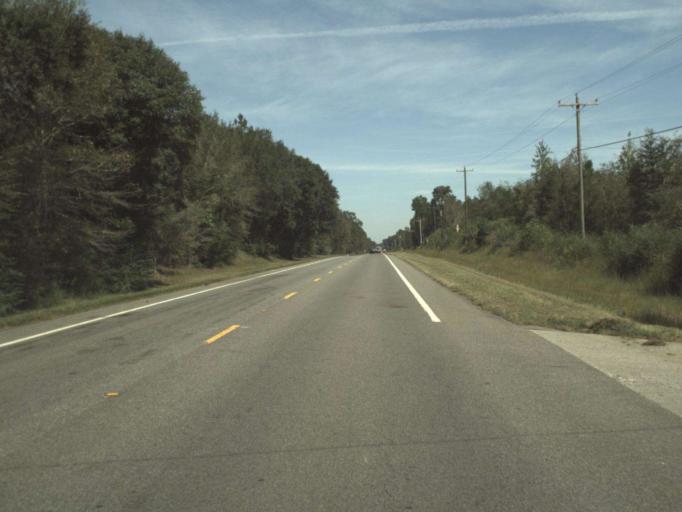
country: US
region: Florida
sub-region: Washington County
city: Chipley
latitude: 30.6846
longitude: -85.5686
